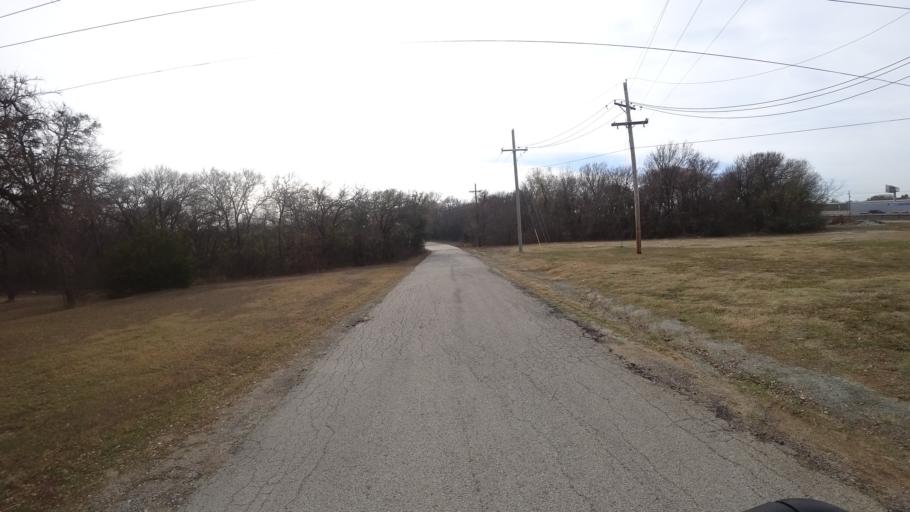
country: US
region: Texas
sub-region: Denton County
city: Highland Village
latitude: 33.0814
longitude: -97.0241
